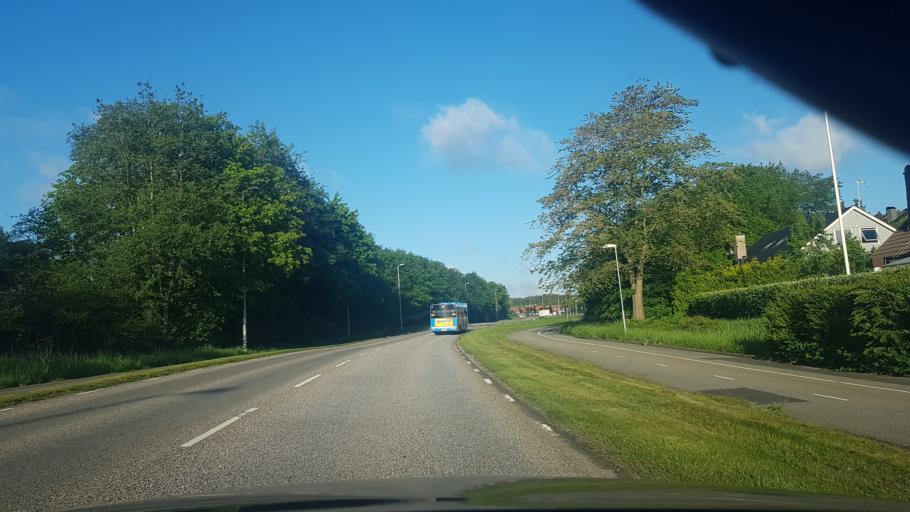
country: SE
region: Vaestra Goetaland
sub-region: Goteborg
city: Majorna
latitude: 57.6352
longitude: 11.9040
